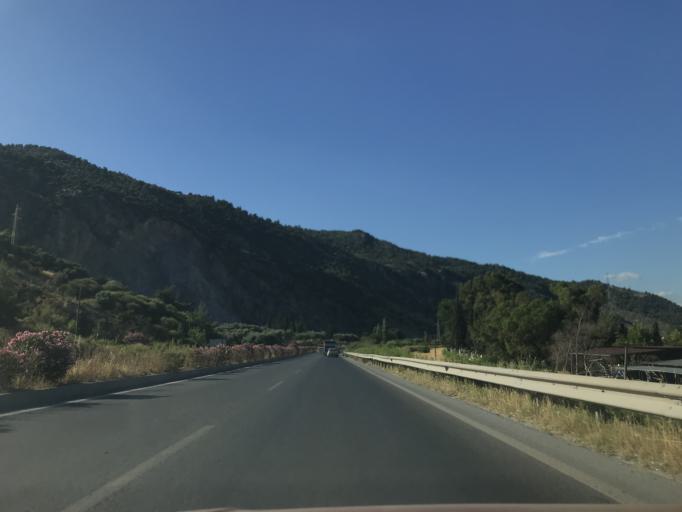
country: TR
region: Aydin
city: Soeke
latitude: 37.7910
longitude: 27.4665
